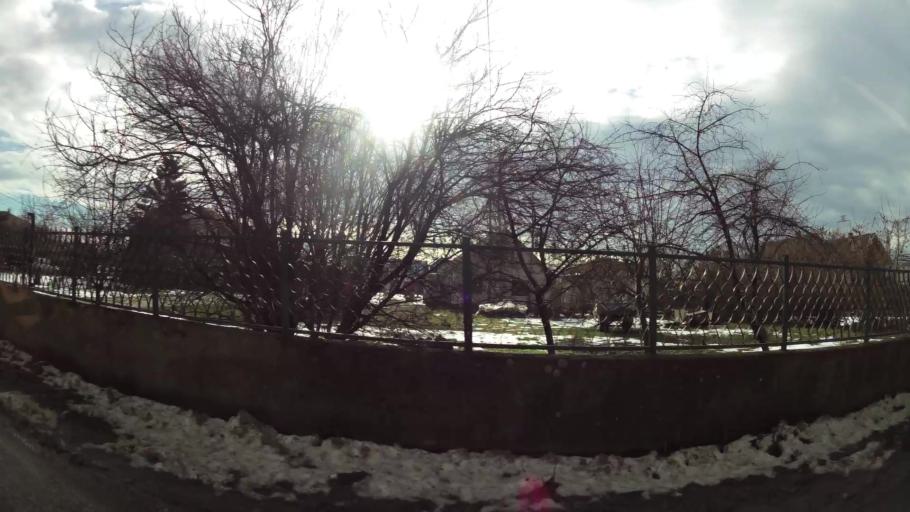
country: RS
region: Central Serbia
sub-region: Belgrade
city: Surcin
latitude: 44.7964
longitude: 20.3417
